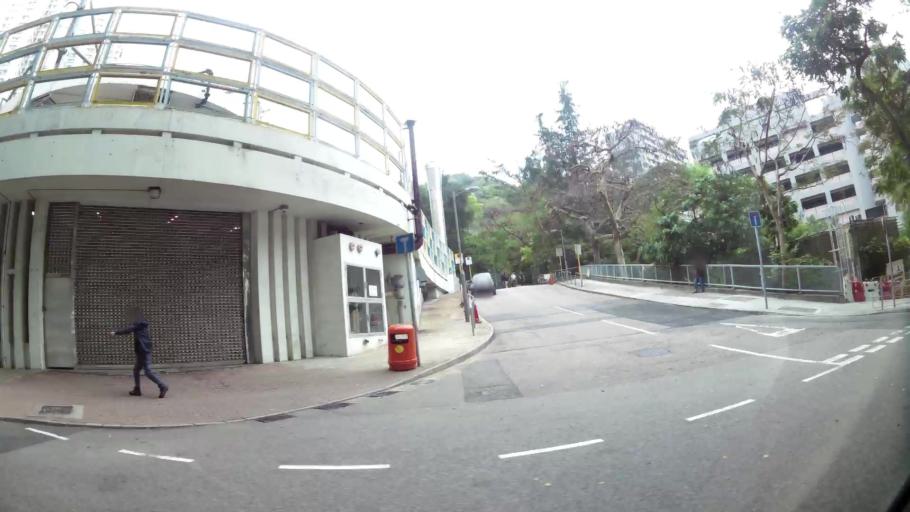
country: HK
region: Wanchai
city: Wan Chai
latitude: 22.2688
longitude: 114.2344
